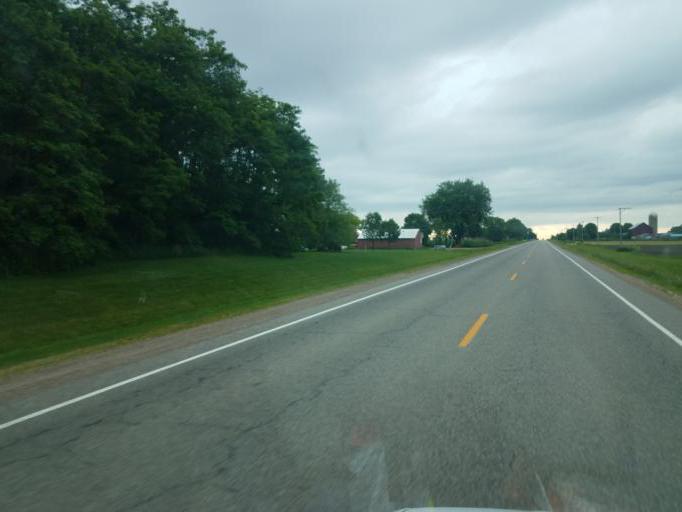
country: US
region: Wisconsin
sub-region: Juneau County
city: Mauston
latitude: 43.7891
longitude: -90.1399
